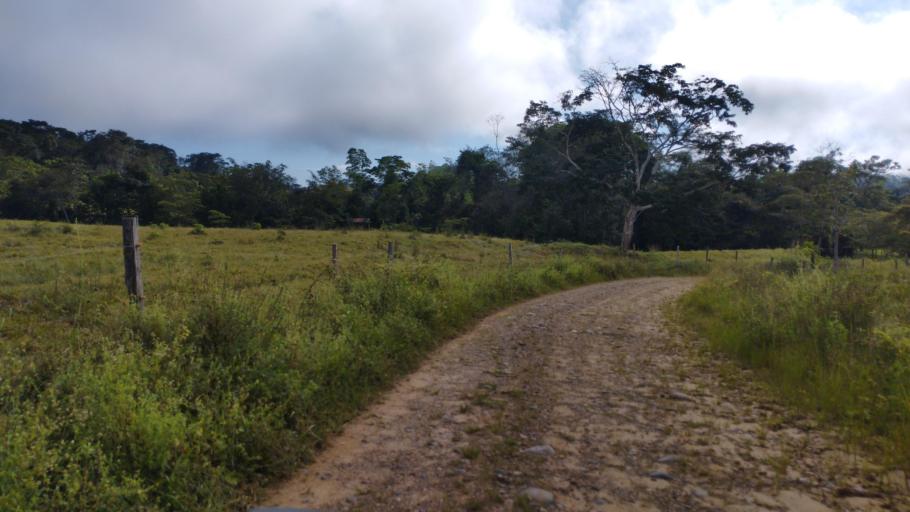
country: CO
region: Casanare
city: Sabanalarga
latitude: 4.7592
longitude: -73.0738
